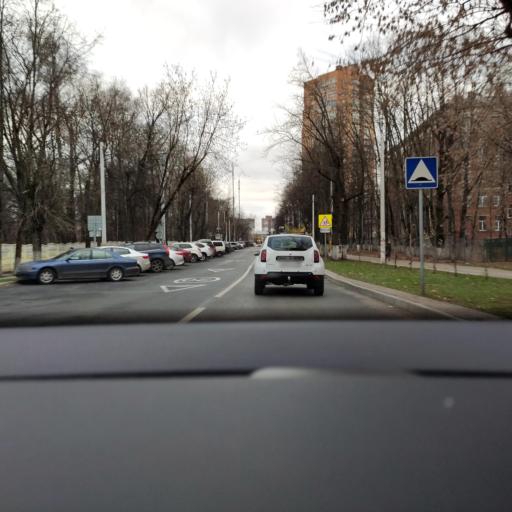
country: RU
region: Moscow
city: Khimki
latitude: 55.8981
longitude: 37.4556
